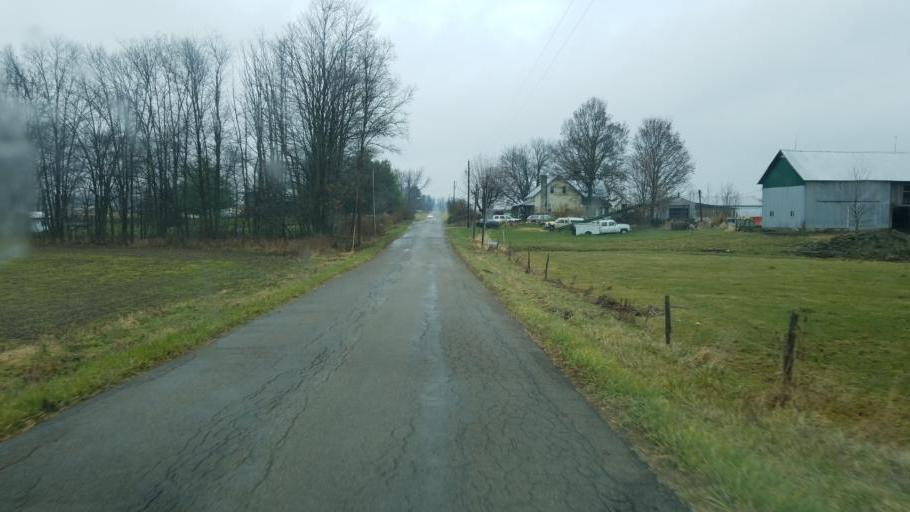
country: US
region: Ohio
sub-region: Knox County
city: Centerburg
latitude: 40.2937
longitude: -82.5724
